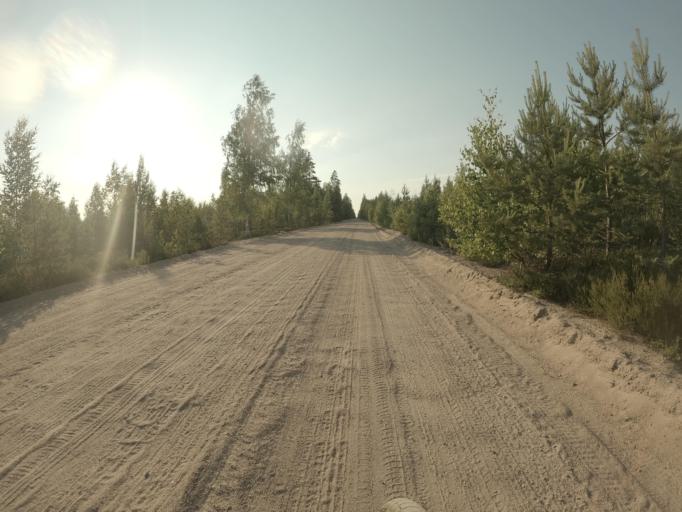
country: RU
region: Leningrad
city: Yakovlevo
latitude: 60.4538
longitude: 29.2539
